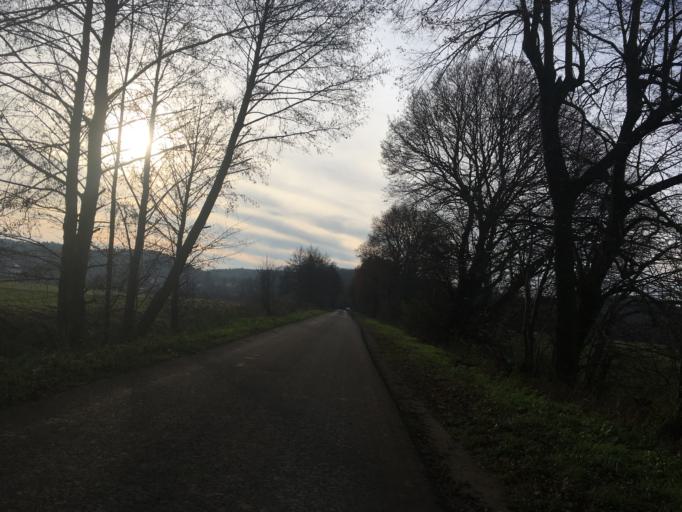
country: DE
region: Brandenburg
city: Falkenberg
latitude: 52.8105
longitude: 13.9657
